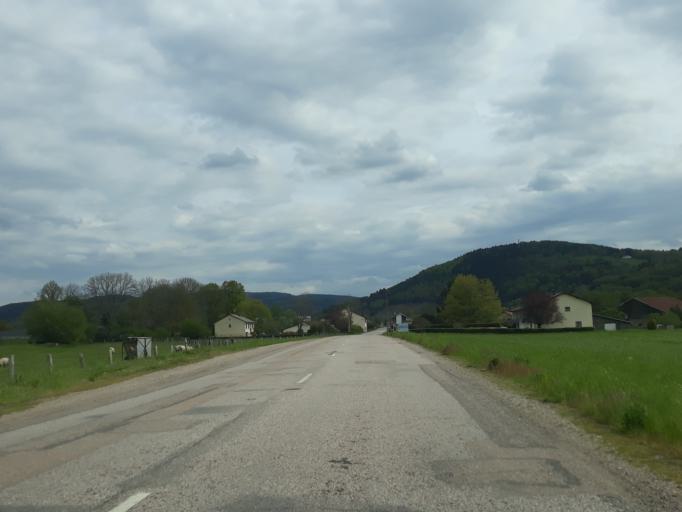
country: FR
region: Lorraine
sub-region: Departement des Vosges
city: Granges-sur-Vologne
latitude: 48.1587
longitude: 6.7783
